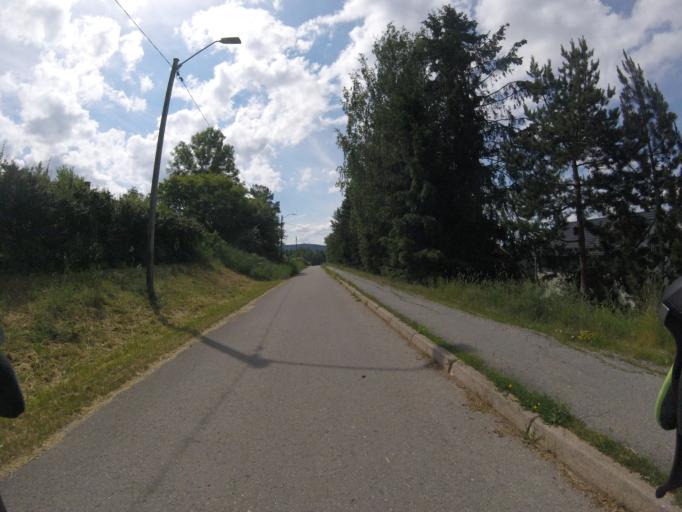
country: NO
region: Akershus
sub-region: Skedsmo
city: Lillestrom
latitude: 59.9698
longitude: 11.0540
